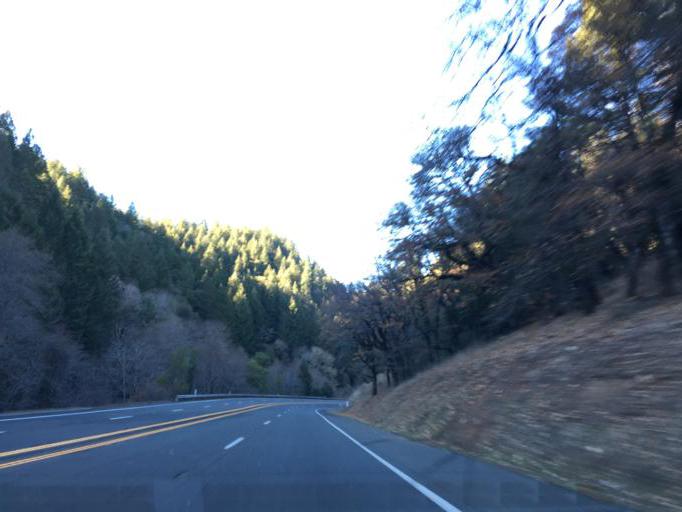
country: US
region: California
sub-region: Mendocino County
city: Laytonville
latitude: 39.5712
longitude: -123.4366
